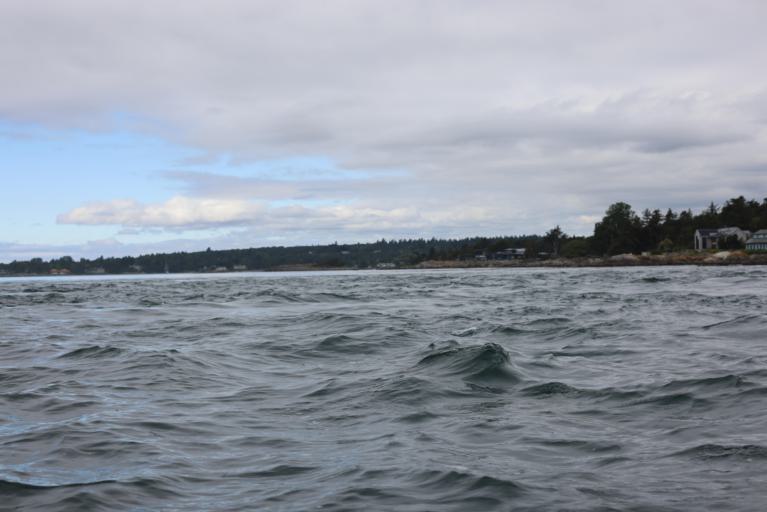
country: CA
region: British Columbia
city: Oak Bay
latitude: 48.4496
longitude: -123.2614
